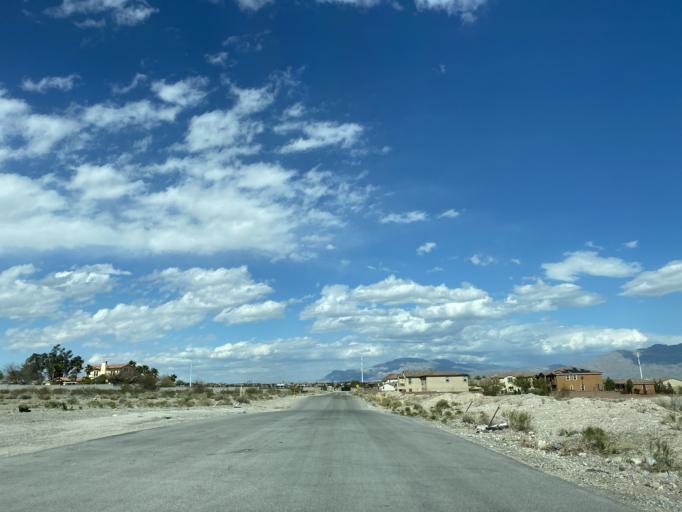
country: US
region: Nevada
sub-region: Clark County
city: Summerlin South
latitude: 36.2486
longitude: -115.3083
